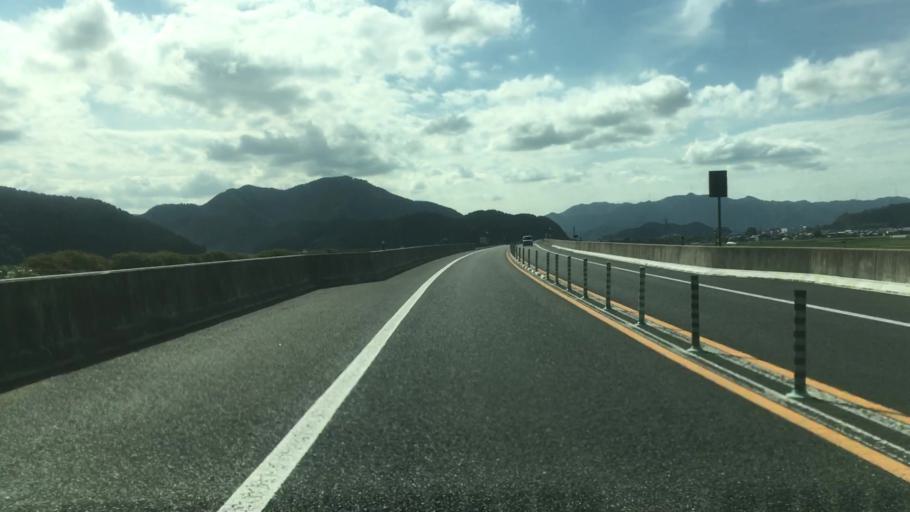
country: JP
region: Kyoto
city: Fukuchiyama
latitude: 35.2017
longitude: 135.0423
